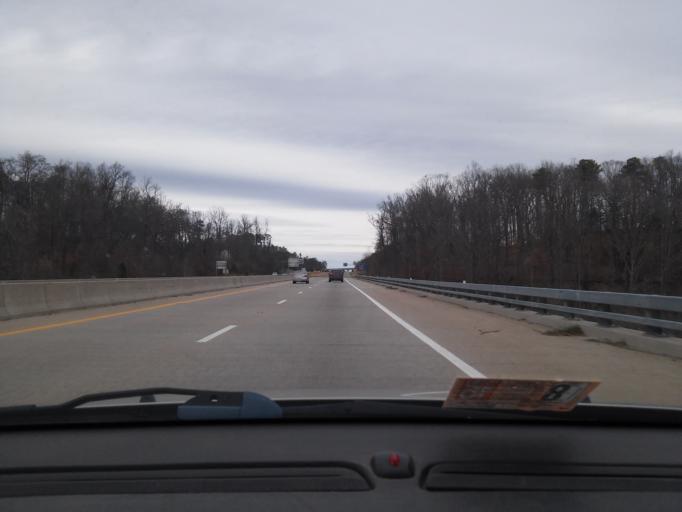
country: US
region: Virginia
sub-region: Henrico County
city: Short Pump
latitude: 37.5769
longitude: -77.6791
